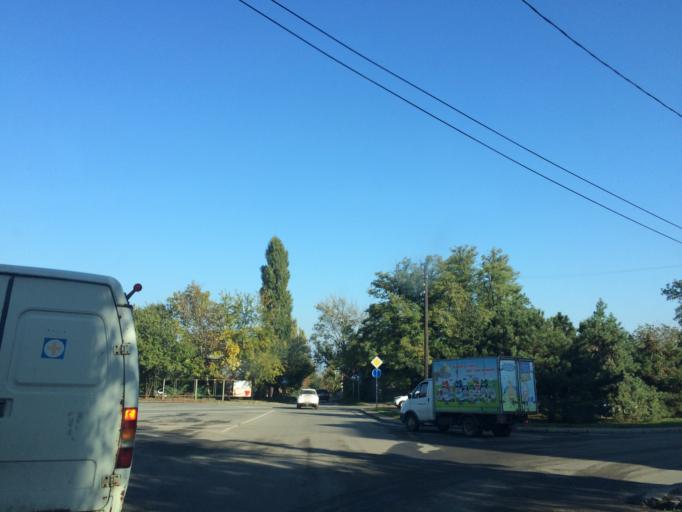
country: RU
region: Rostov
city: Rostov-na-Donu
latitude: 47.2153
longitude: 39.6635
